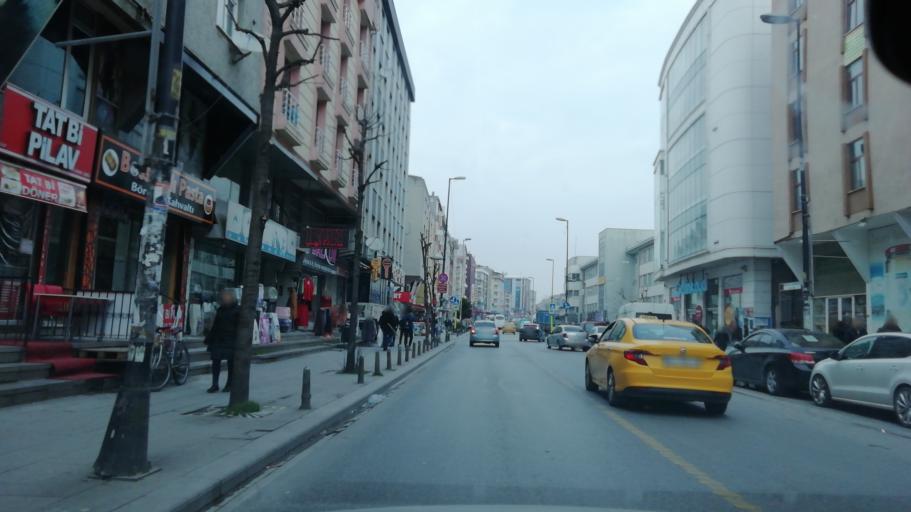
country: TR
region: Istanbul
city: Bahcelievler
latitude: 41.0104
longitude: 28.8414
